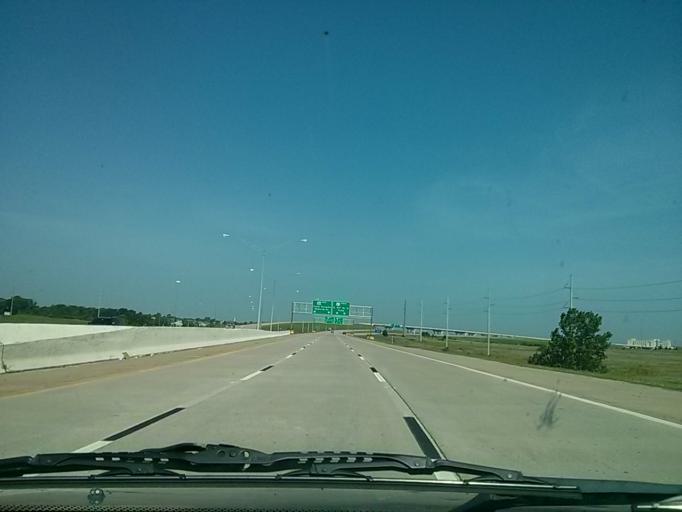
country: US
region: Oklahoma
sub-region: Tulsa County
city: Broken Arrow
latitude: 36.0254
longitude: -95.8523
